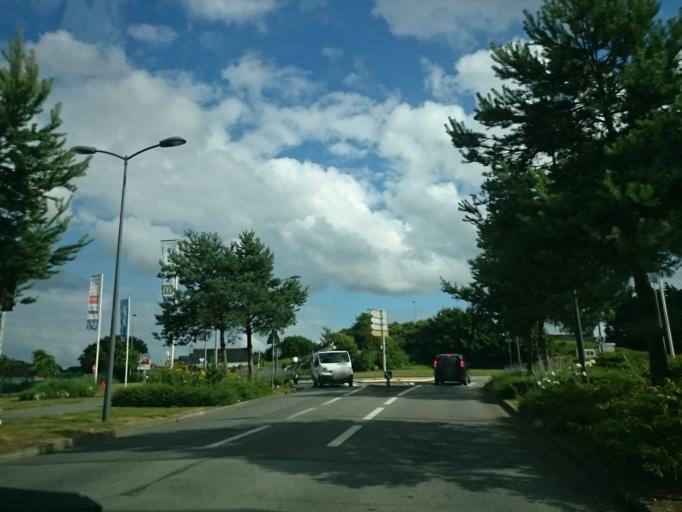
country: FR
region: Brittany
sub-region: Departement du Finistere
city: Le Relecq-Kerhuon
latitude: 48.4154
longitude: -4.4381
